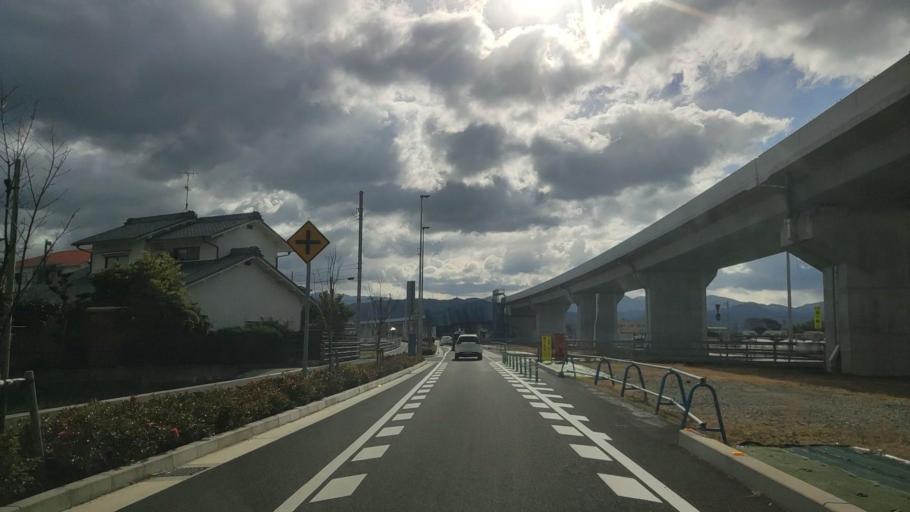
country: JP
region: Ehime
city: Masaki-cho
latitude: 33.8148
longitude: 132.7206
